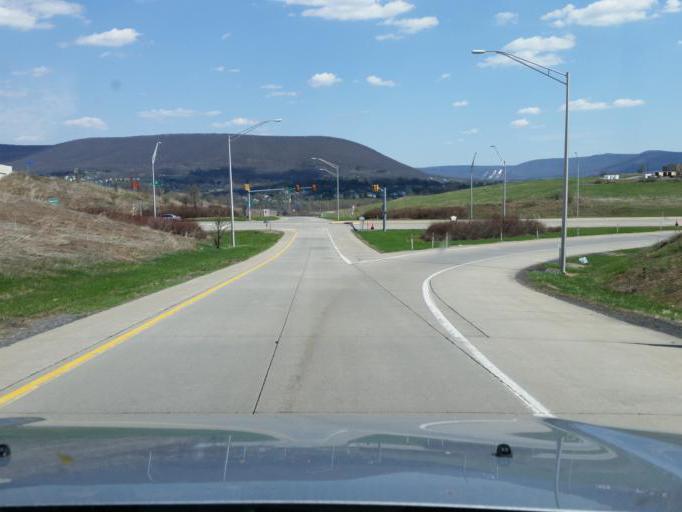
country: US
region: Pennsylvania
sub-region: Centre County
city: Houserville
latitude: 40.8244
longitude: -77.8474
